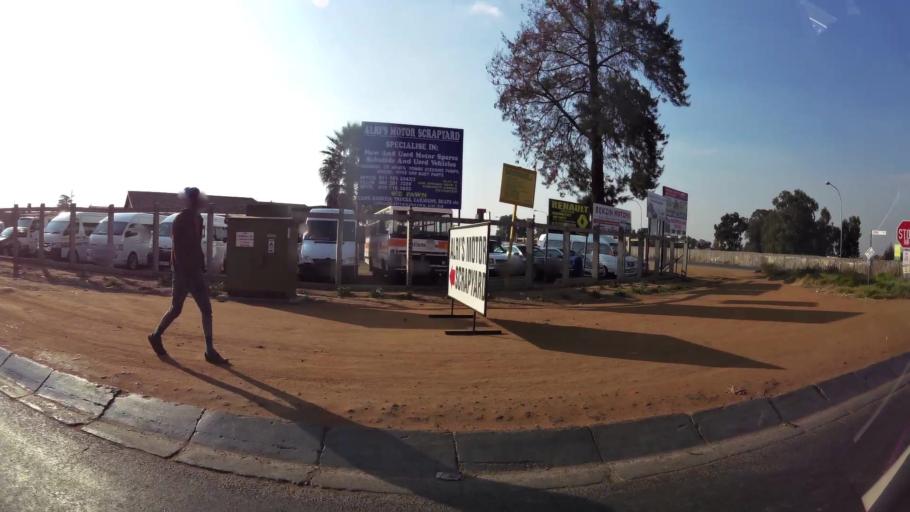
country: ZA
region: Gauteng
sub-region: Ekurhuleni Metropolitan Municipality
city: Benoni
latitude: -26.1317
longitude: 28.3891
